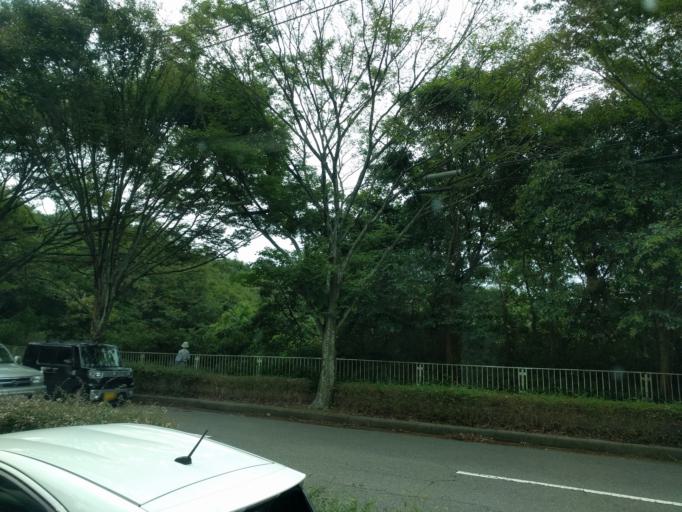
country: JP
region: Hyogo
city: Kobe
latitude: 34.7106
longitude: 135.1212
